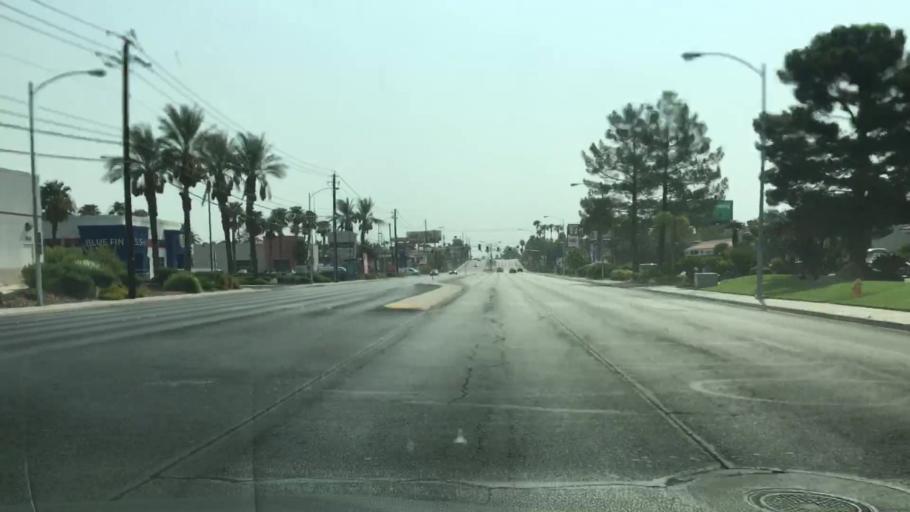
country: US
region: Nevada
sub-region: Clark County
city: Whitney
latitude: 36.0711
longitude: -115.0895
